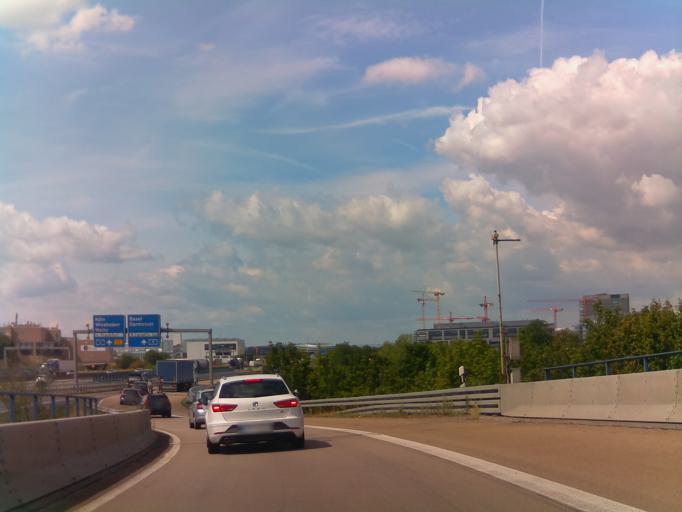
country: DE
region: Hesse
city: Niederrad
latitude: 50.0537
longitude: 8.6089
